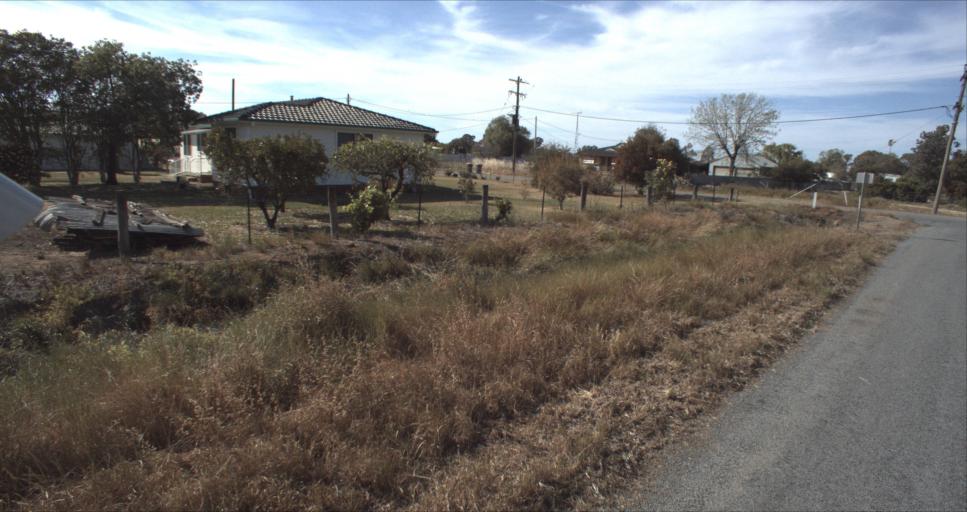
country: AU
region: New South Wales
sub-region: Leeton
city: Leeton
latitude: -34.6020
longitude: 146.4133
